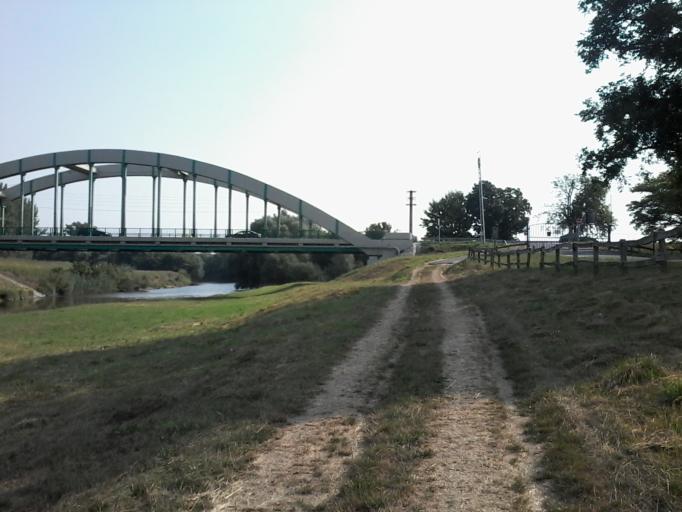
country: HU
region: Vas
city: Sarvar
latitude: 47.2456
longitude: 16.9533
